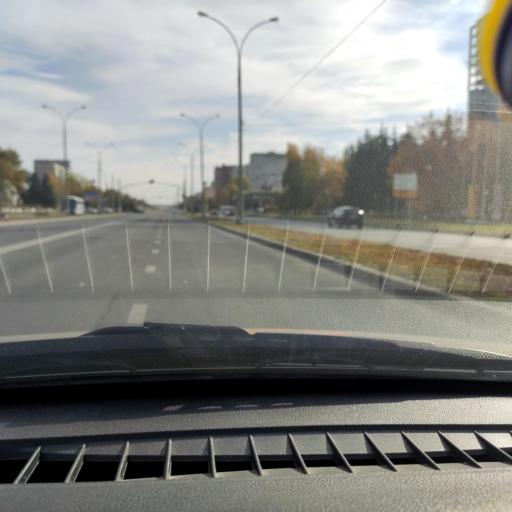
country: RU
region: Samara
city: Tol'yatti
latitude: 53.5278
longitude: 49.2935
